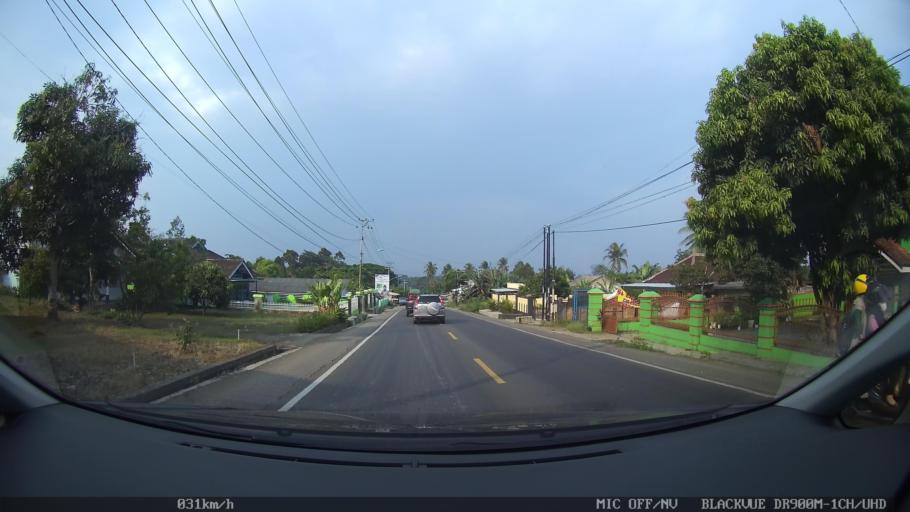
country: ID
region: Lampung
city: Natar
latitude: -5.3667
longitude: 105.1809
